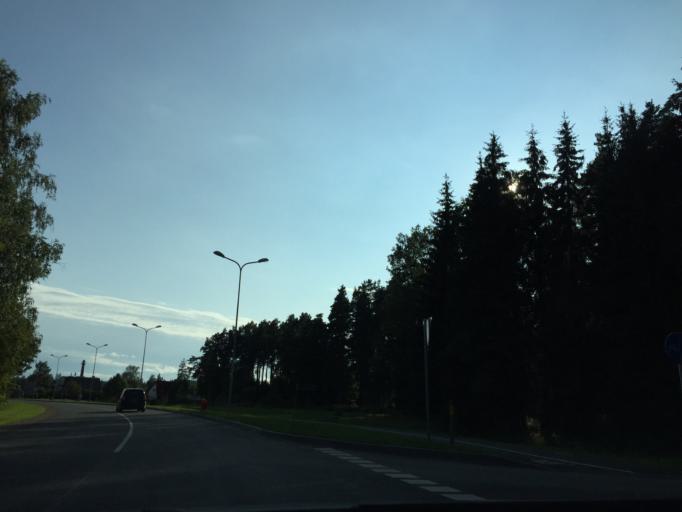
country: LV
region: Ogre
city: Ogre
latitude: 56.8187
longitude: 24.6542
